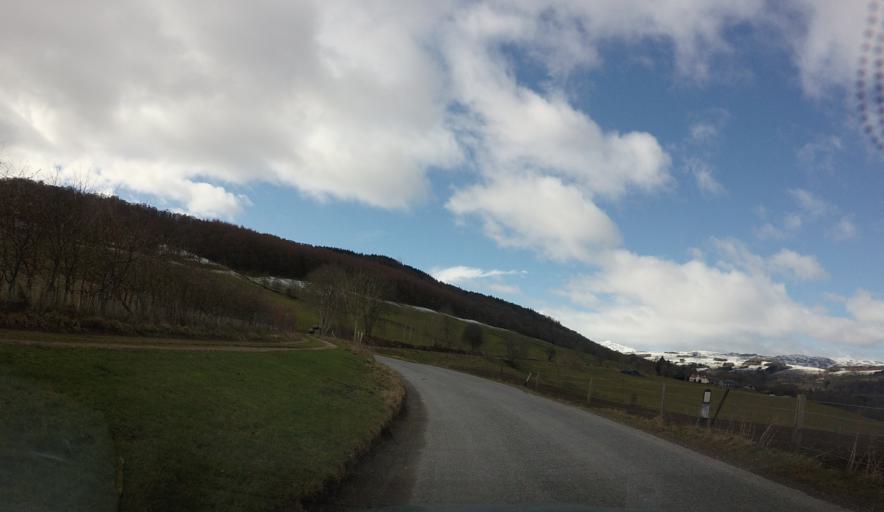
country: GB
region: Scotland
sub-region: Perth and Kinross
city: Pitlochry
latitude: 56.6476
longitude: -3.7261
